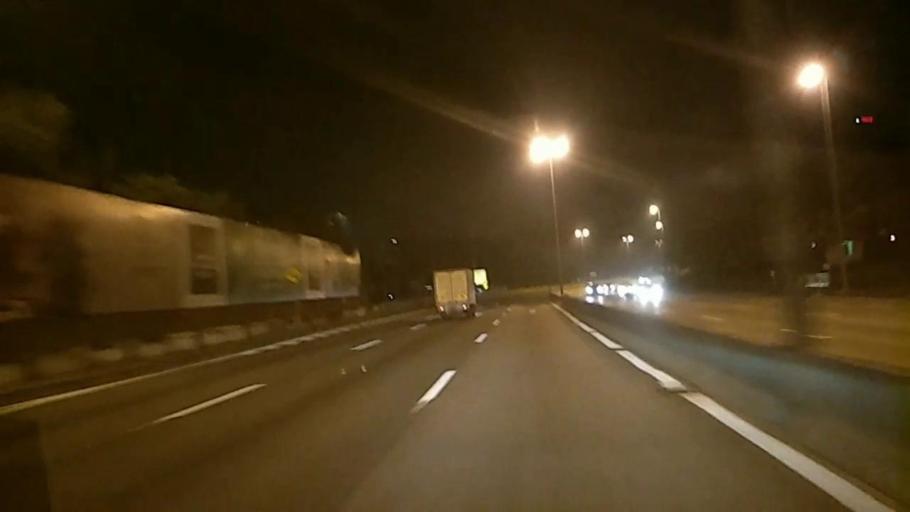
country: MY
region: Selangor
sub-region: Petaling
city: Petaling Jaya
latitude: 3.0969
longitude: 101.5992
